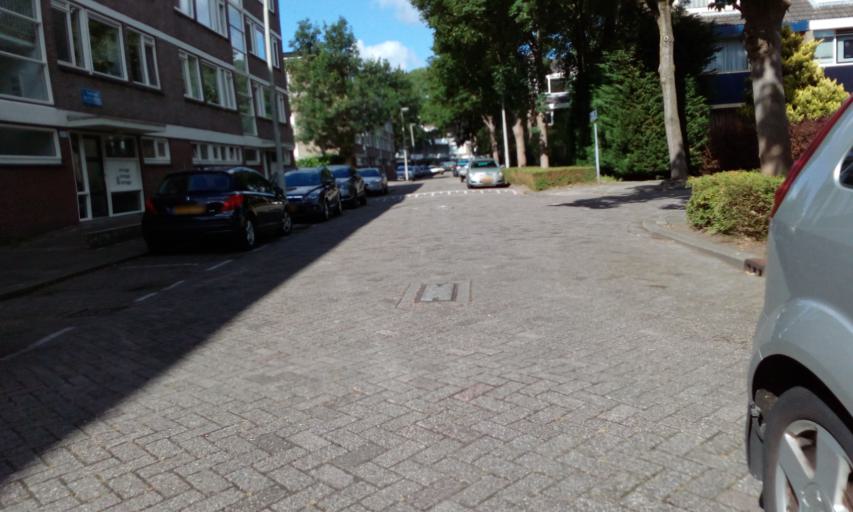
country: NL
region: South Holland
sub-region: Gemeente Rotterdam
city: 's-Gravenland
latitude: 51.9390
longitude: 4.5427
